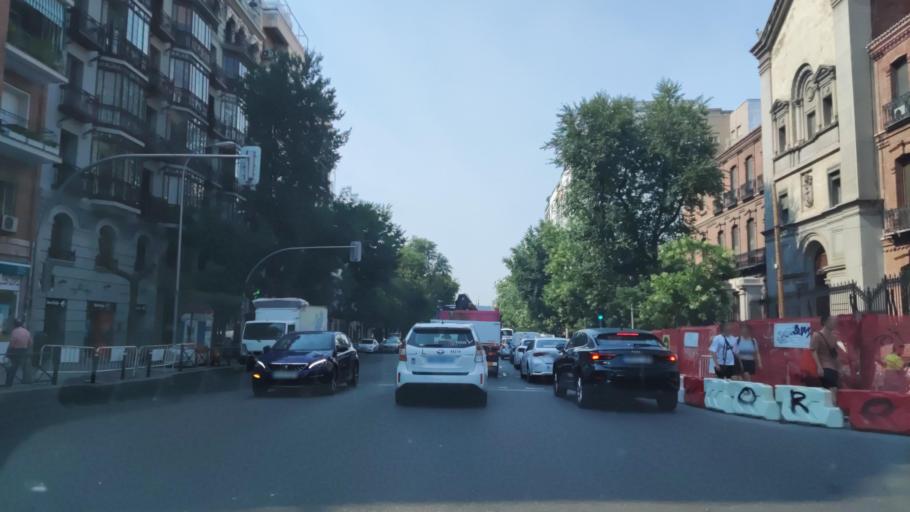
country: ES
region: Madrid
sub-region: Provincia de Madrid
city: Chamberi
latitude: 40.4315
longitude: -3.7052
